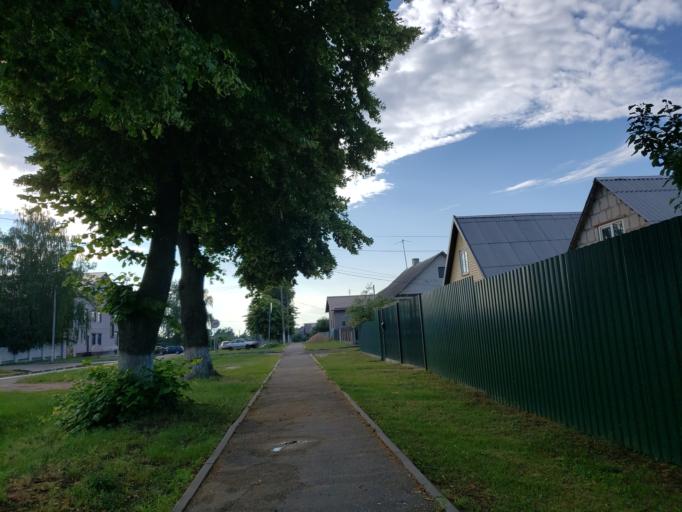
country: BY
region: Minsk
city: Chervyen'
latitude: 53.7053
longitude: 28.4362
